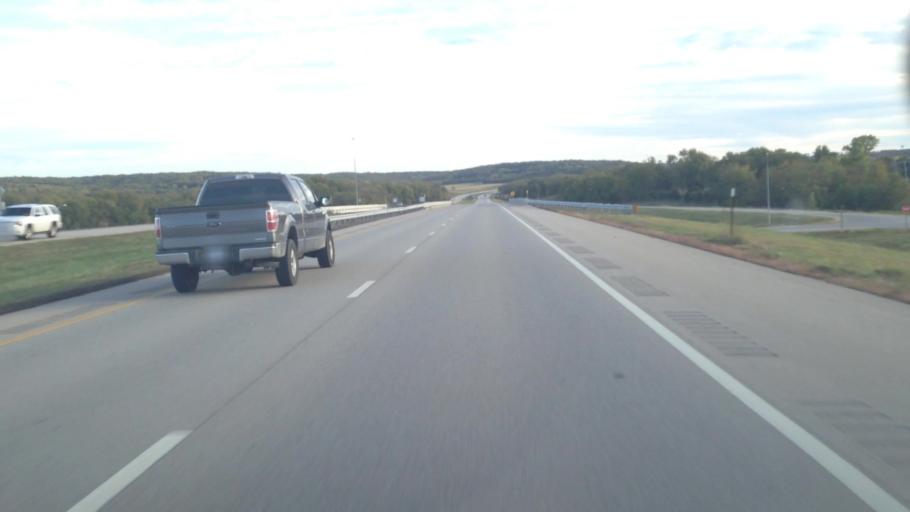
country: US
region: Kansas
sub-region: Douglas County
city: Lawrence
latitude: 38.8859
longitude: -95.2589
